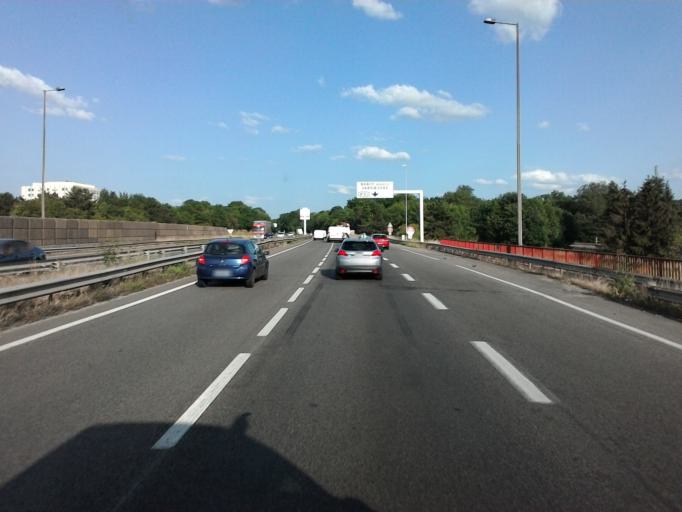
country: FR
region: Lorraine
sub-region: Departement de Meurthe-et-Moselle
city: Chavigny
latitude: 48.6466
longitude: 6.1397
